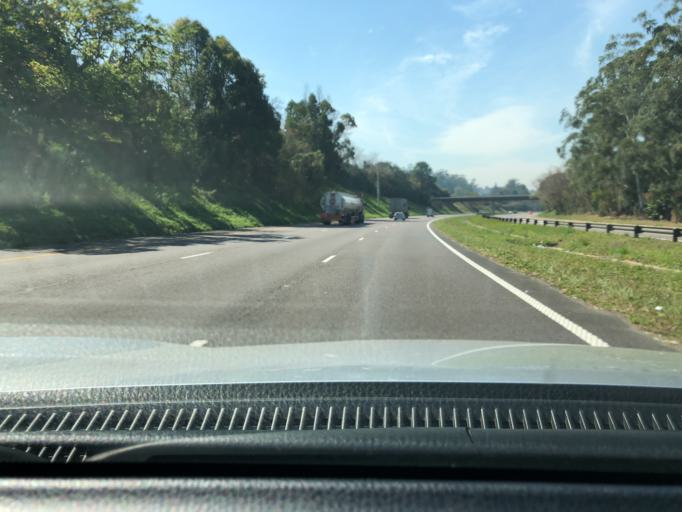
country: ZA
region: KwaZulu-Natal
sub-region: eThekwini Metropolitan Municipality
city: Berea
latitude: -29.8347
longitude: 30.8805
